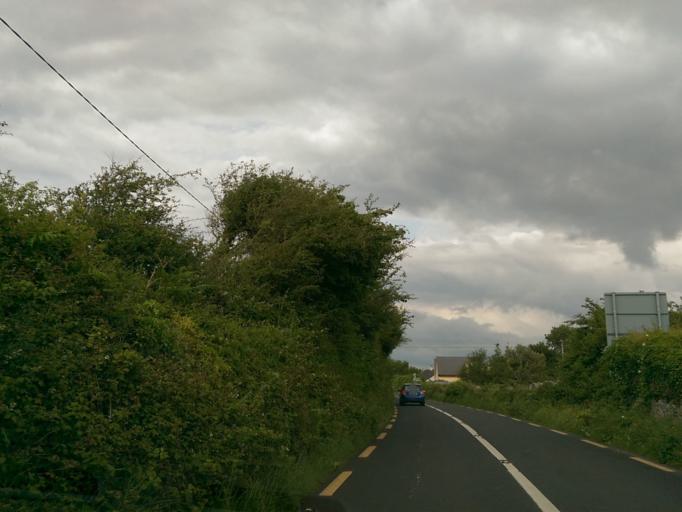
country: IE
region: Connaught
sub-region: County Galway
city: Bearna
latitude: 53.1051
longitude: -9.1572
